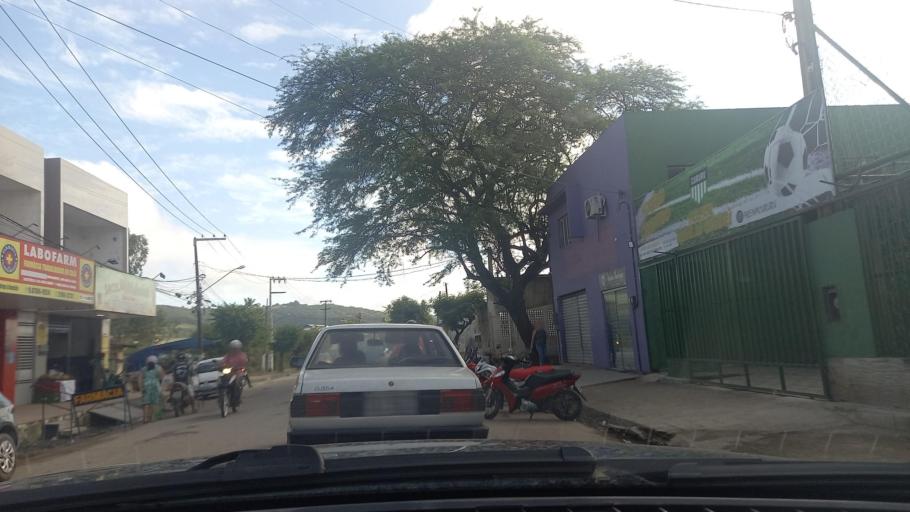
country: BR
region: Pernambuco
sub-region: Vitoria De Santo Antao
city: Vitoria de Santo Antao
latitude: -8.1053
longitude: -35.2834
